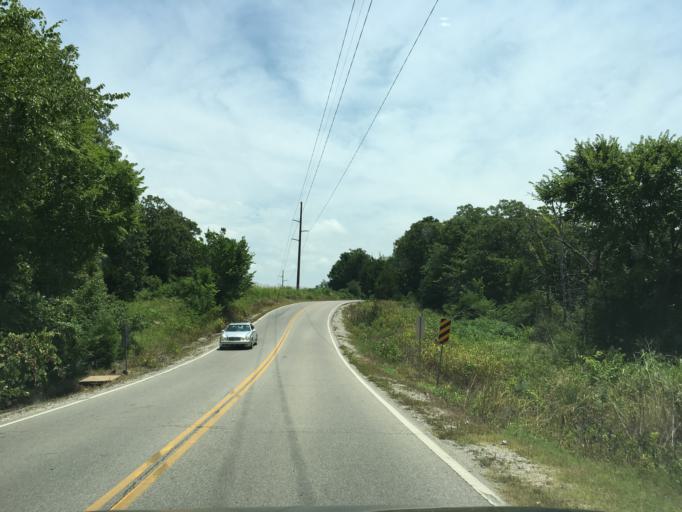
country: US
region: Oklahoma
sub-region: Tulsa County
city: Jenks
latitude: 36.0752
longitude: -96.0016
